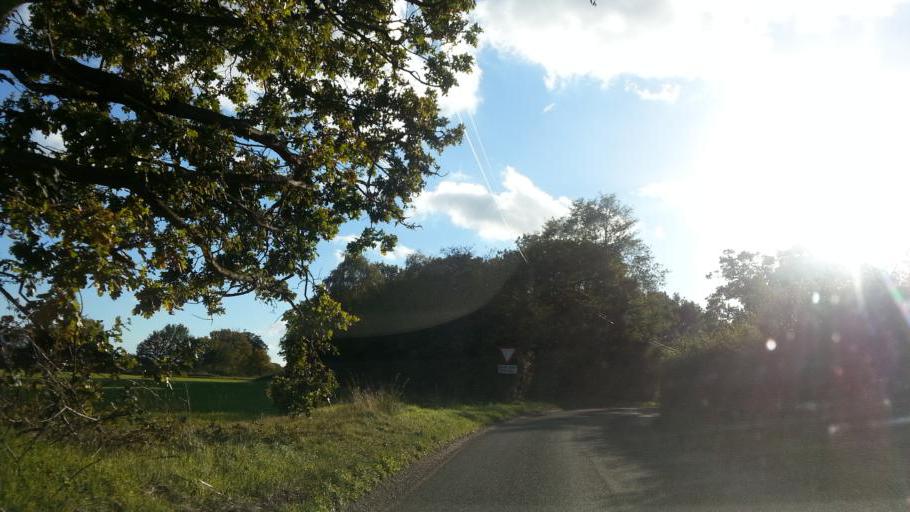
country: GB
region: England
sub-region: Suffolk
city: Thurston
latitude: 52.2343
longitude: 0.8068
